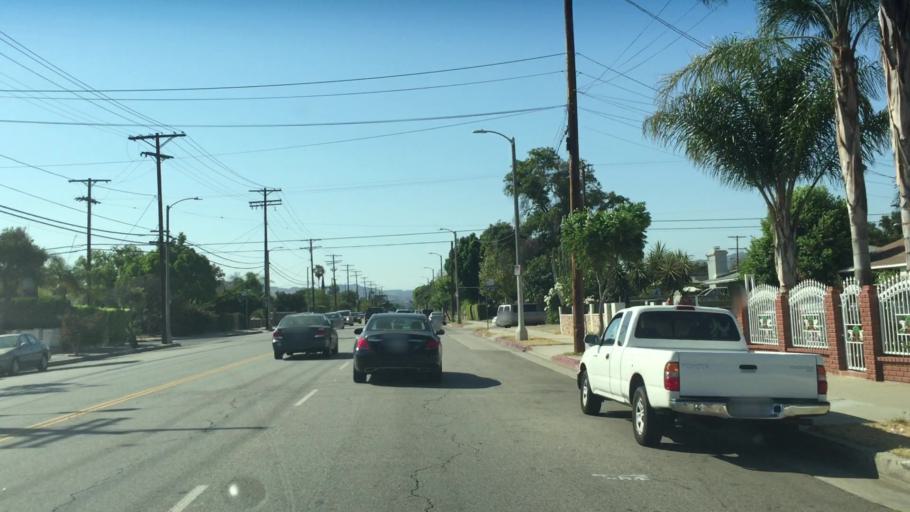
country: US
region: California
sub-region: Los Angeles County
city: San Fernando
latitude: 34.2447
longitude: -118.4287
